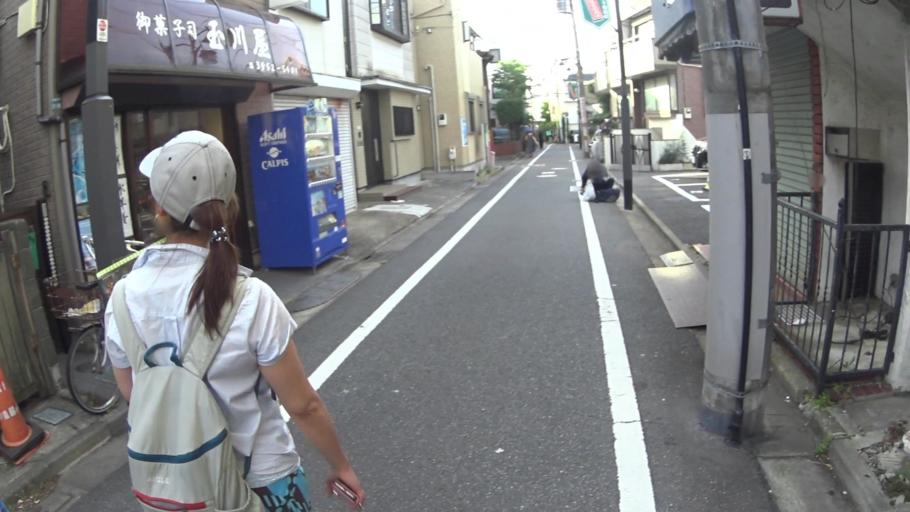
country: JP
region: Tokyo
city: Tokyo
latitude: 35.7306
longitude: 139.6817
